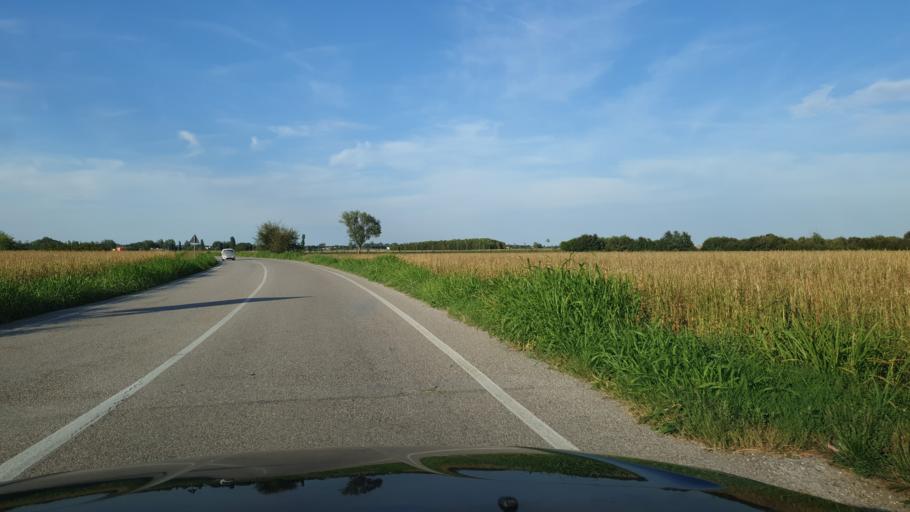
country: IT
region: Veneto
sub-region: Provincia di Rovigo
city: Pincara
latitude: 44.9897
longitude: 11.6128
